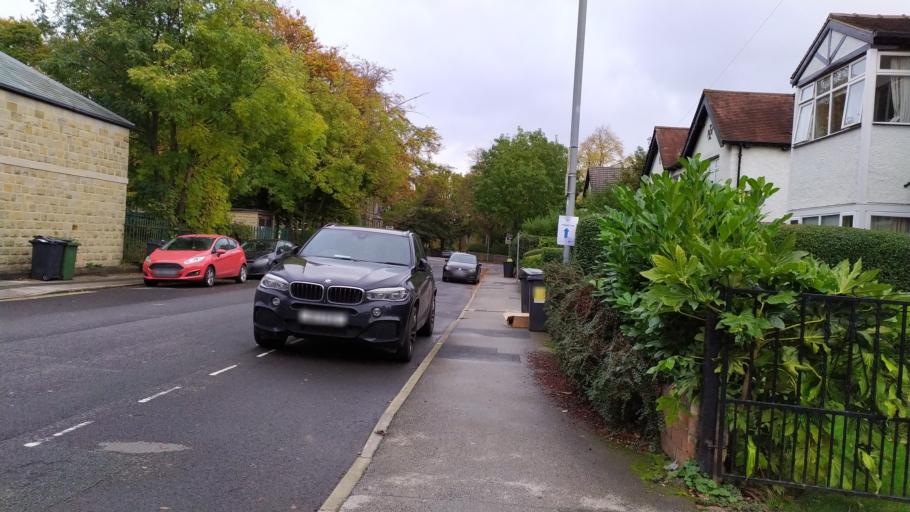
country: GB
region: England
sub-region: City and Borough of Leeds
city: Chapel Allerton
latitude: 53.8298
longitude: -1.5871
